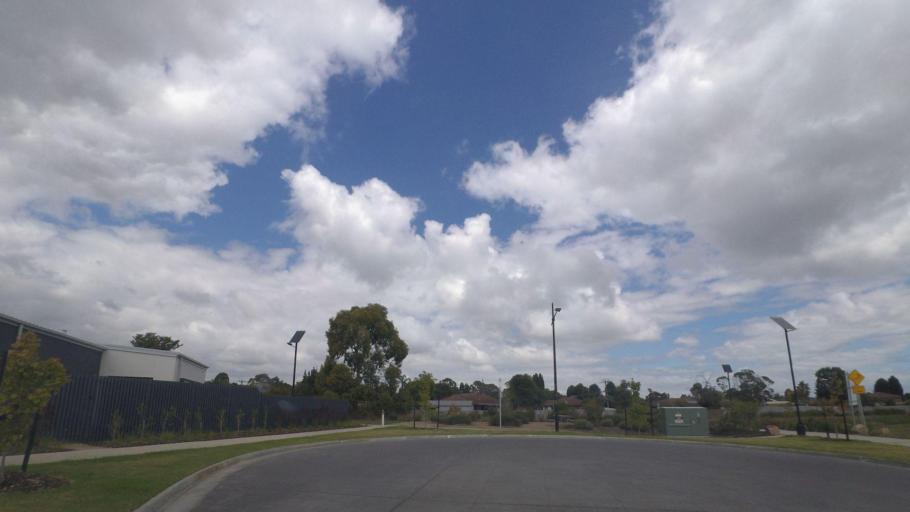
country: AU
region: Victoria
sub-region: Knox
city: Scoresby
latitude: -37.9160
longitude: 145.2279
